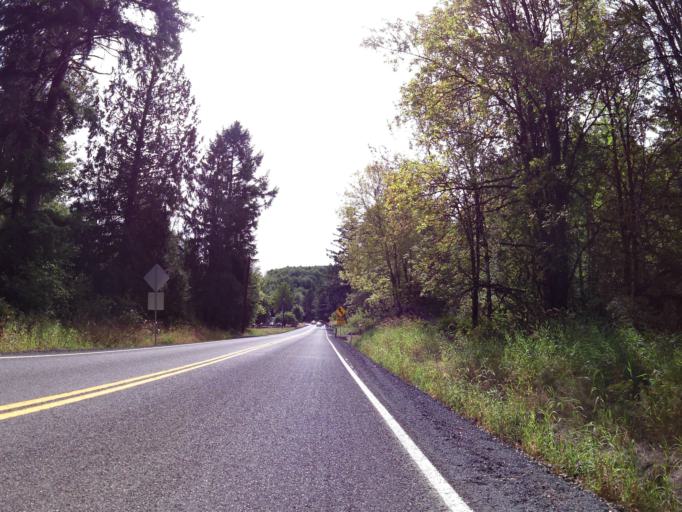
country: US
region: Washington
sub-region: Lewis County
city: Napavine
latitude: 46.5647
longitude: -122.9658
